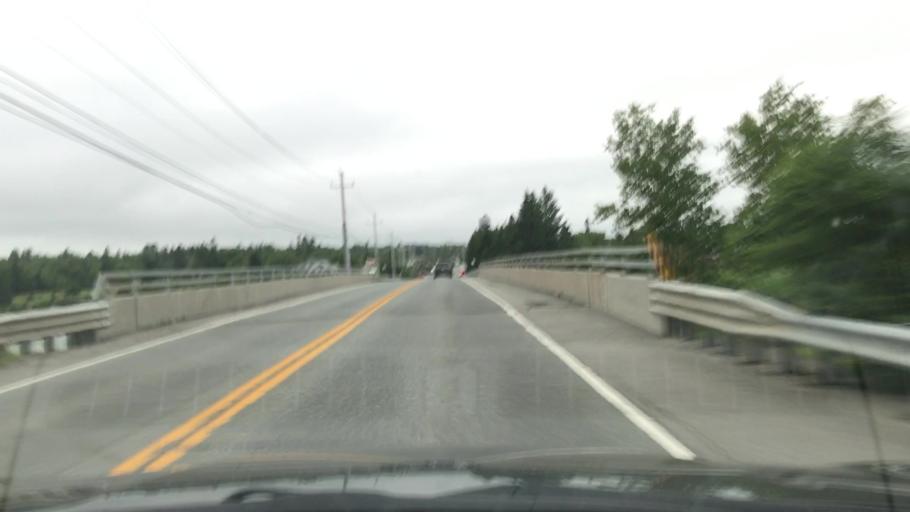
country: US
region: Maine
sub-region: Hancock County
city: Trenton
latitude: 44.4296
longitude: -68.3673
